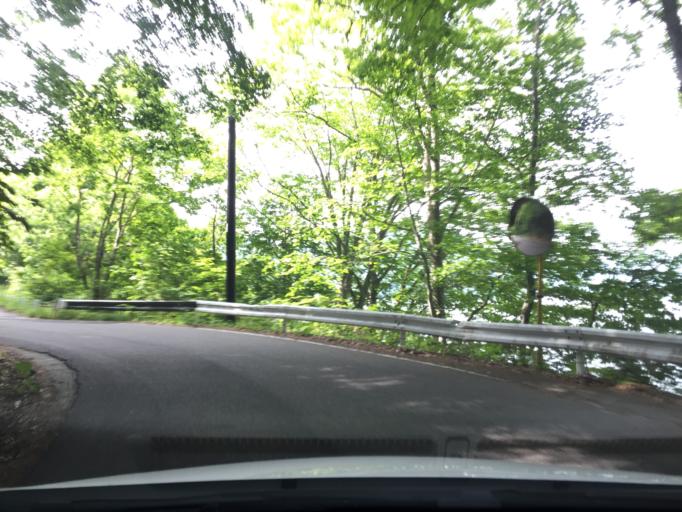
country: JP
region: Fukushima
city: Inawashiro
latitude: 37.7105
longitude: 140.0463
